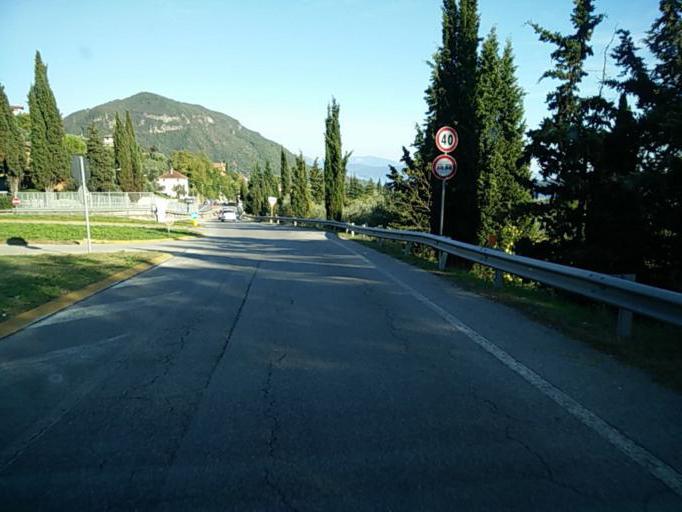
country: IT
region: Lombardy
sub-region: Provincia di Brescia
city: Roe Volciano
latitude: 45.6120
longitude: 10.4857
